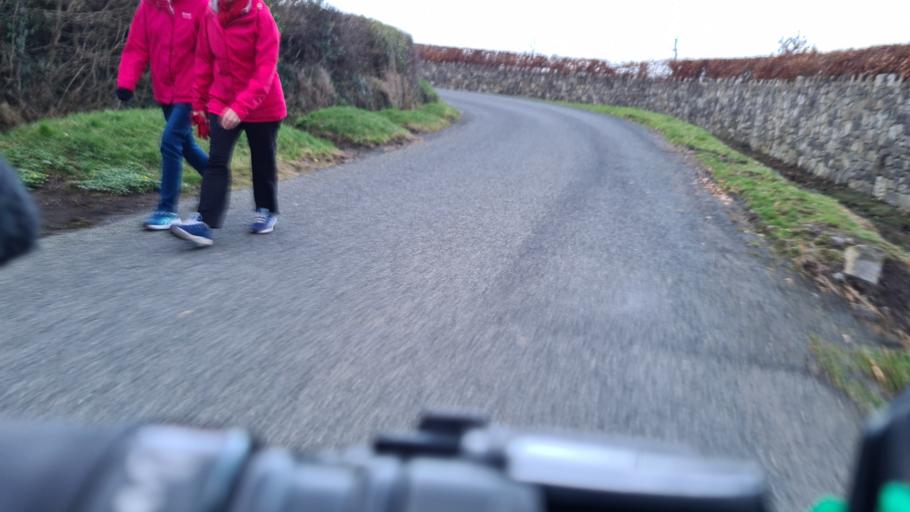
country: IE
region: Leinster
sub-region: Kildare
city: Maynooth
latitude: 53.3392
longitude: -6.5958
